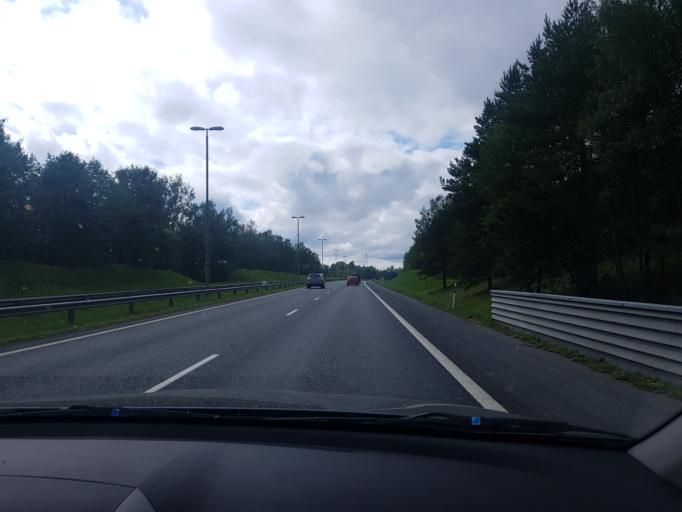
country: FI
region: Haeme
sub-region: Haemeenlinna
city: Haemeenlinna
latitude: 61.0039
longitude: 24.4441
